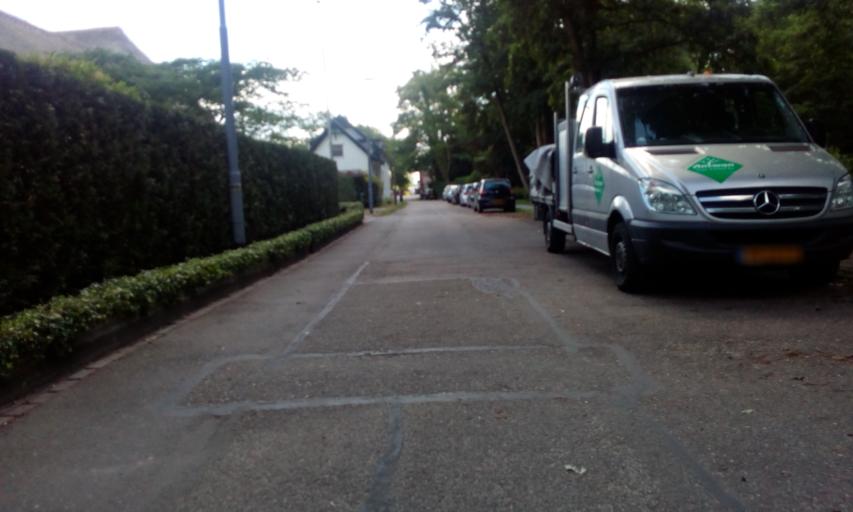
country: NL
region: South Holland
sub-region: Gemeente Rotterdam
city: Rotterdam
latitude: 51.9549
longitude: 4.4904
